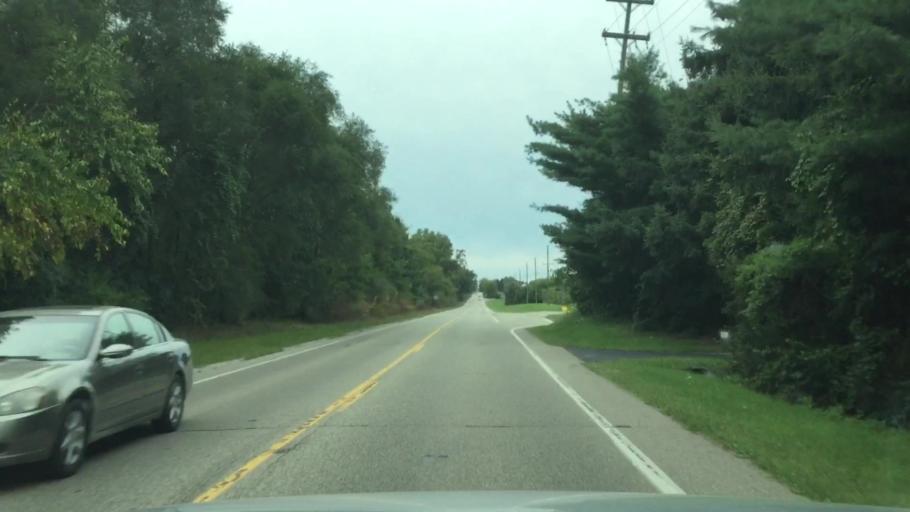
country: US
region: Michigan
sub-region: Washtenaw County
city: Ypsilanti
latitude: 42.2160
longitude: -83.6601
